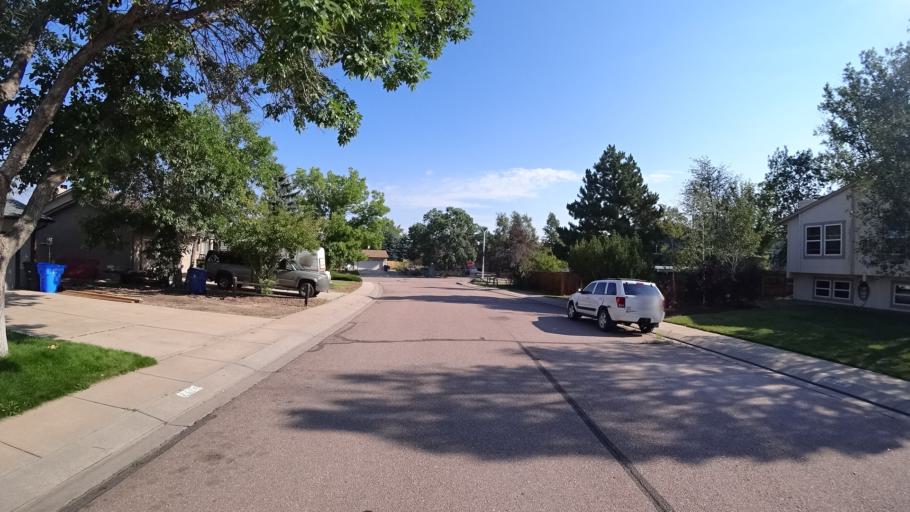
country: US
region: Colorado
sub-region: El Paso County
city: Black Forest
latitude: 38.9438
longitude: -104.7700
